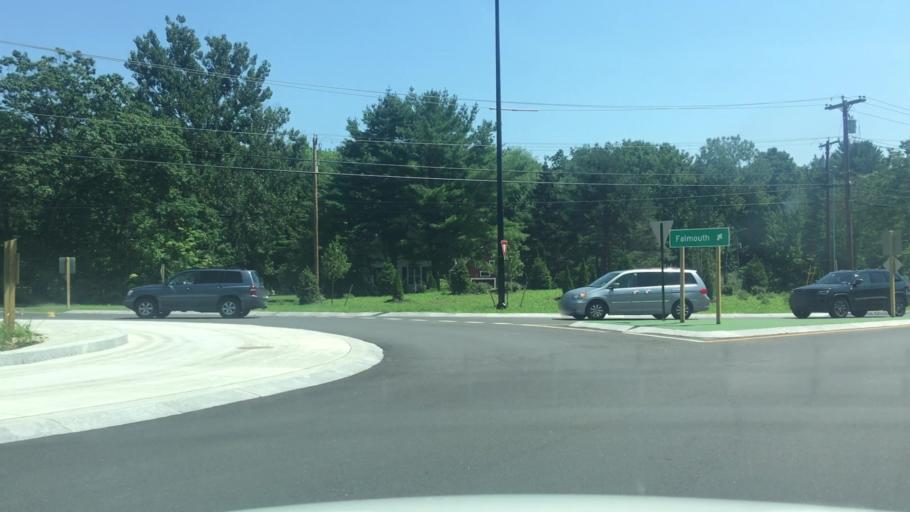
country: US
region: Maine
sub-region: Cumberland County
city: Falmouth
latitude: 43.7351
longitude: -70.2376
